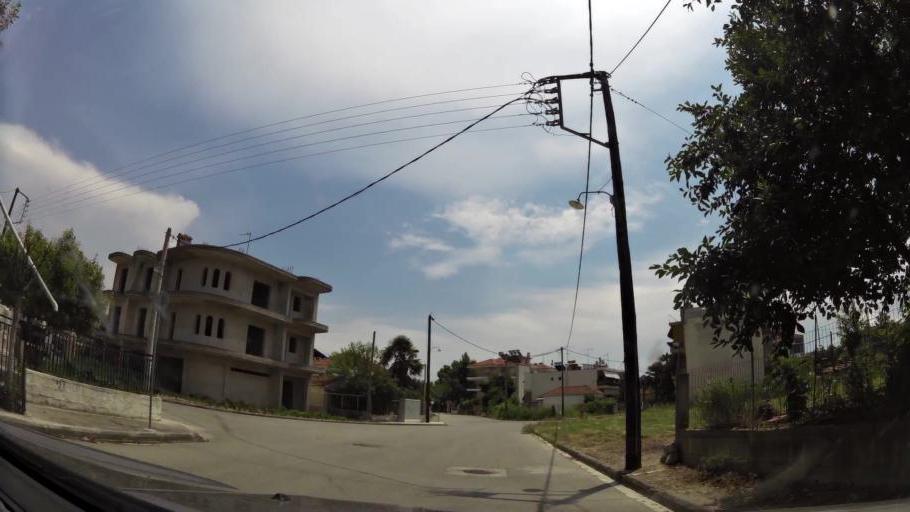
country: GR
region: Central Macedonia
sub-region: Nomos Pierias
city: Peristasi
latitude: 40.2725
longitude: 22.5291
